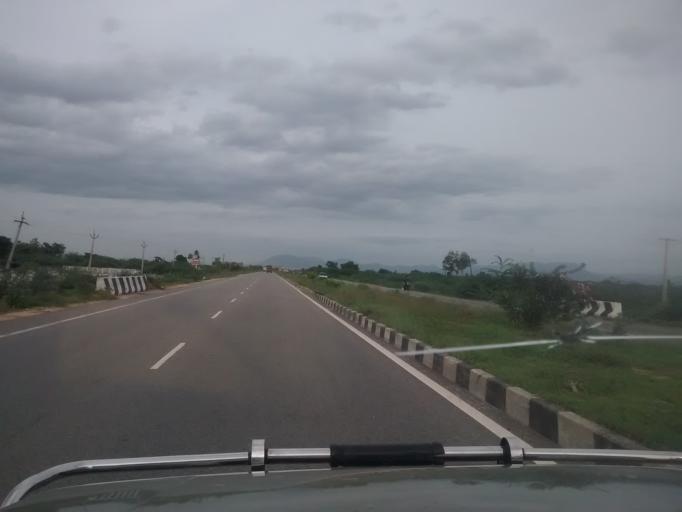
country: IN
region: Andhra Pradesh
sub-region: Chittoor
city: Tirupati
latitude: 13.6037
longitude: 79.3770
